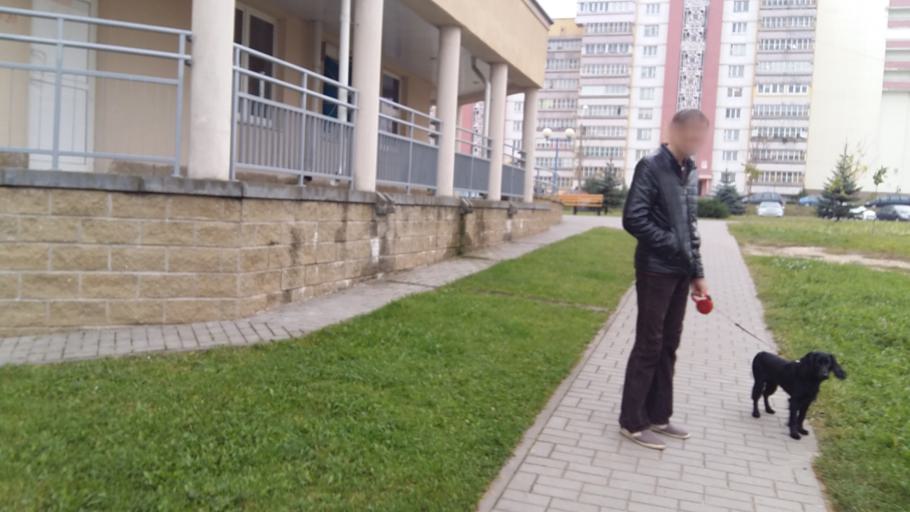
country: BY
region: Grodnenskaya
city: Hrodna
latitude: 53.7104
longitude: 23.8507
